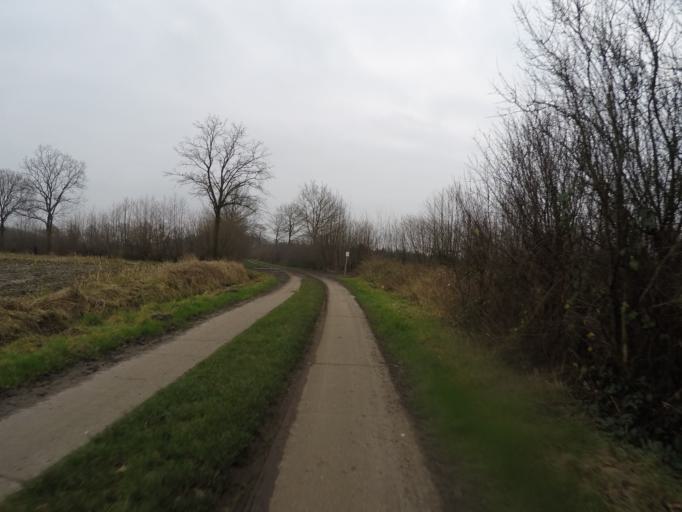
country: DE
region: Schleswig-Holstein
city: Borstel-Hohenraden
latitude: 53.7055
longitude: 9.8438
